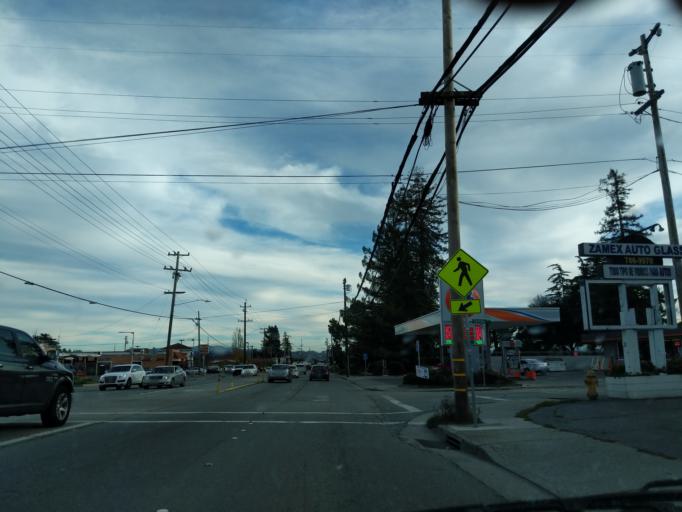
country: US
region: California
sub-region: Santa Cruz County
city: Freedom
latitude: 36.9320
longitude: -121.7700
